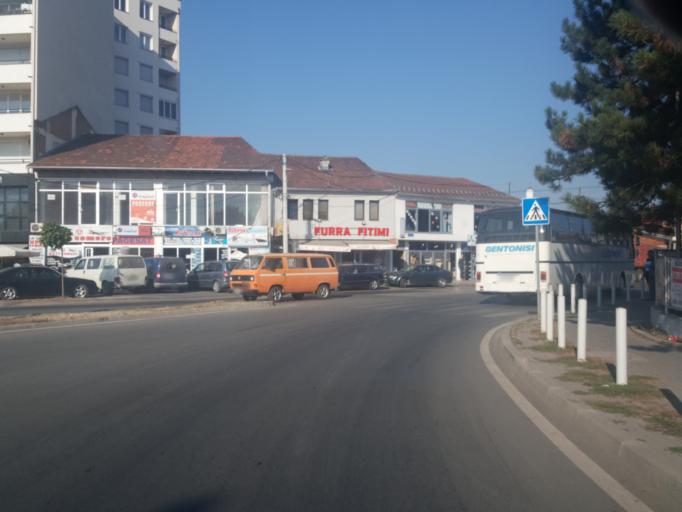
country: XK
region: Gjakova
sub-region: Komuna e Gjakoves
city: Gjakove
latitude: 42.3872
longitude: 20.4333
